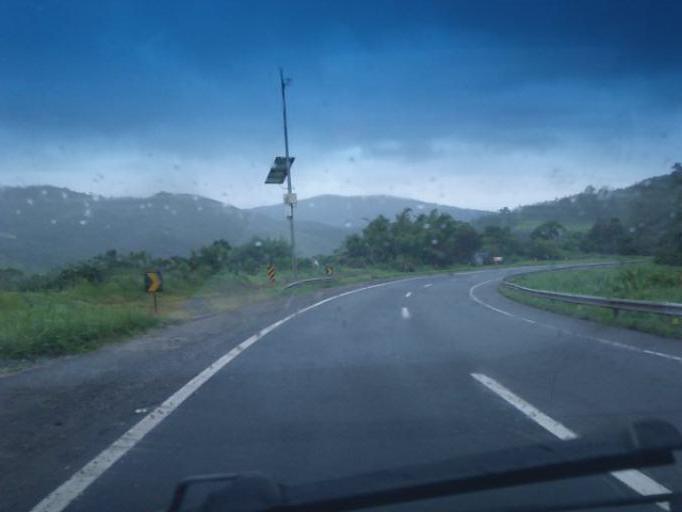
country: BR
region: Sao Paulo
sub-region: Cajati
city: Cajati
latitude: -24.8708
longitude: -48.2107
